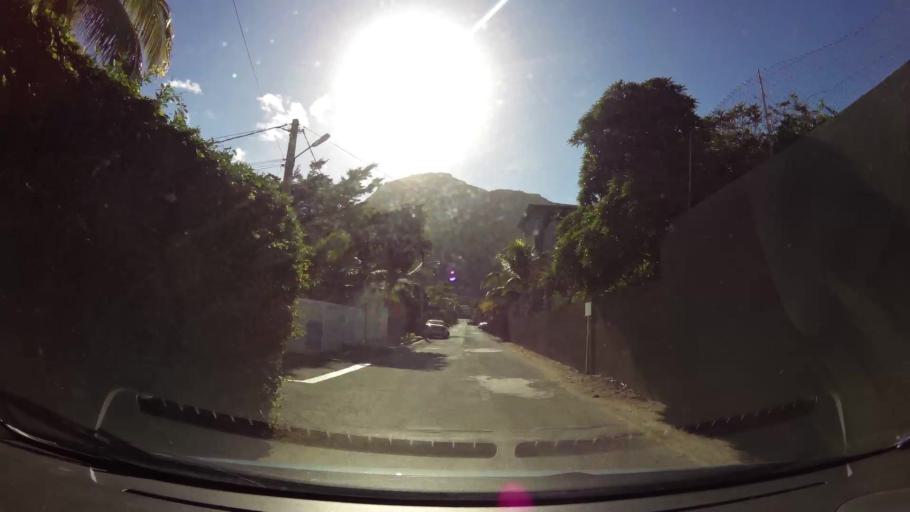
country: MU
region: Black River
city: Grande Riviere Noire
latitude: -20.3572
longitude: 57.3650
